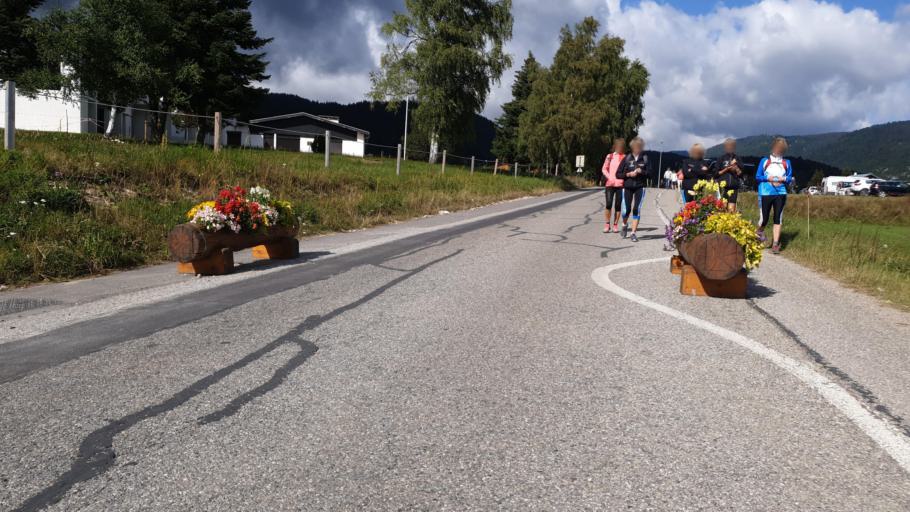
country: FR
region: Rhone-Alpes
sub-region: Departement de l'Isere
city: Autrans
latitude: 45.1769
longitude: 5.5405
